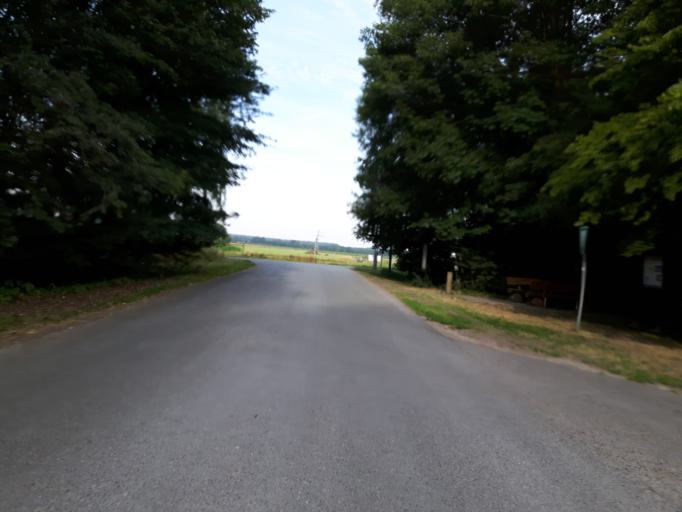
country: DE
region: Lower Saxony
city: Delmenhorst
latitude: 53.0866
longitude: 8.6173
